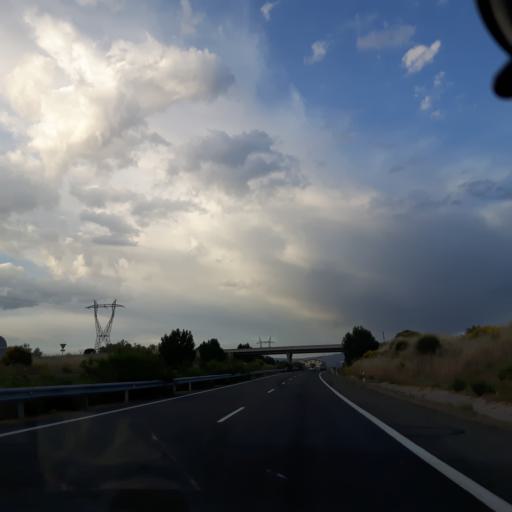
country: ES
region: Castille and Leon
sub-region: Provincia de Salamanca
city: Fuentes de Bejar
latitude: 40.5003
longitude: -5.6759
